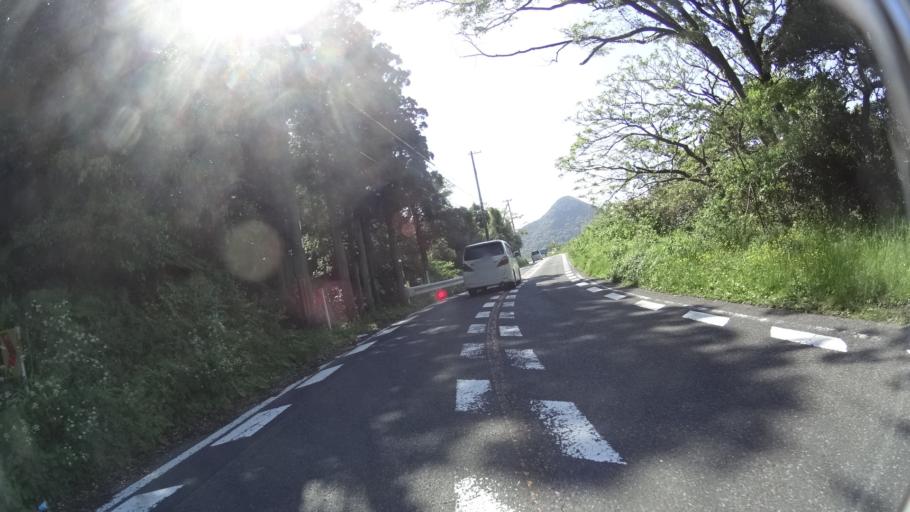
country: JP
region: Kyoto
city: Miyazu
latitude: 35.7508
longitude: 135.1530
